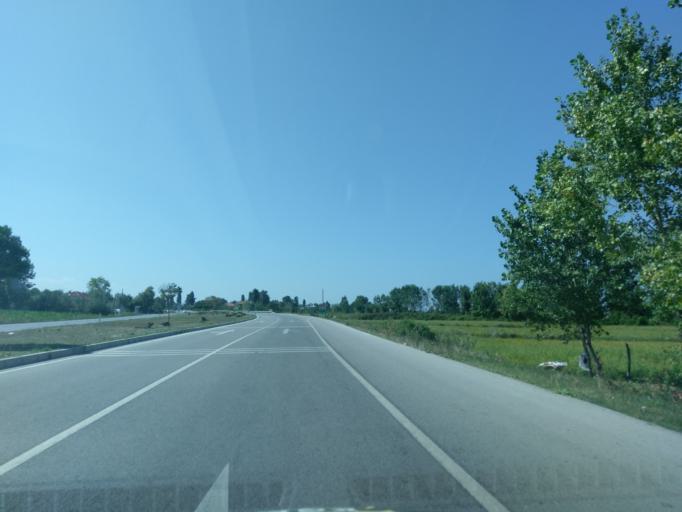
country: TR
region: Samsun
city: Alacam
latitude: 41.6117
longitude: 35.7139
